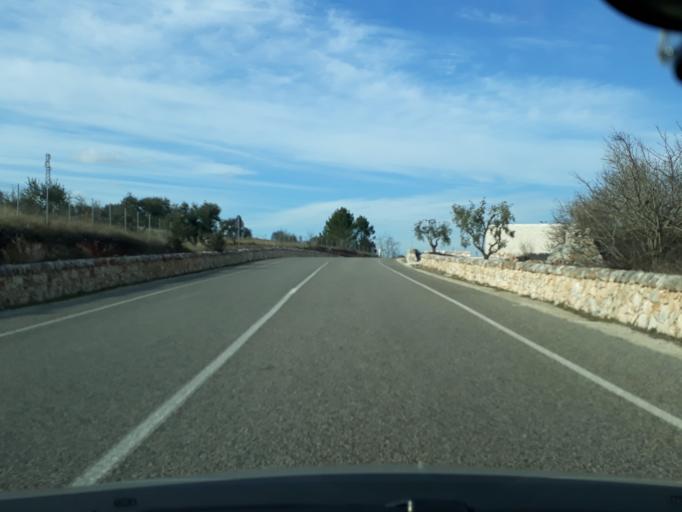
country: IT
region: Apulia
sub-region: Provincia di Bari
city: Locorotondo
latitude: 40.7533
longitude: 17.3449
